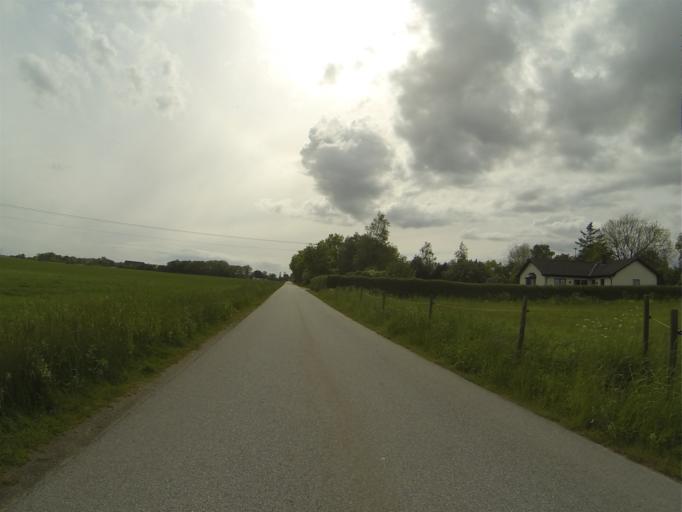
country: SE
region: Skane
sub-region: Lunds Kommun
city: Lund
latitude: 55.6990
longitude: 13.3043
